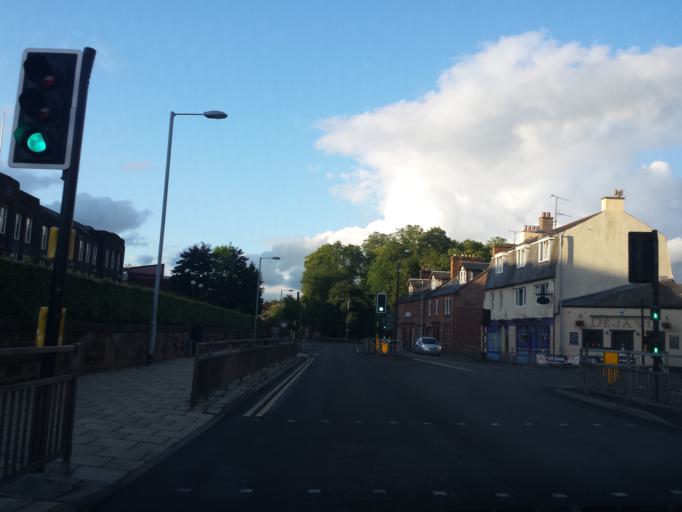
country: GB
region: Scotland
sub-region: Dumfries and Galloway
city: Dumfries
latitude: 55.0712
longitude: -3.6113
